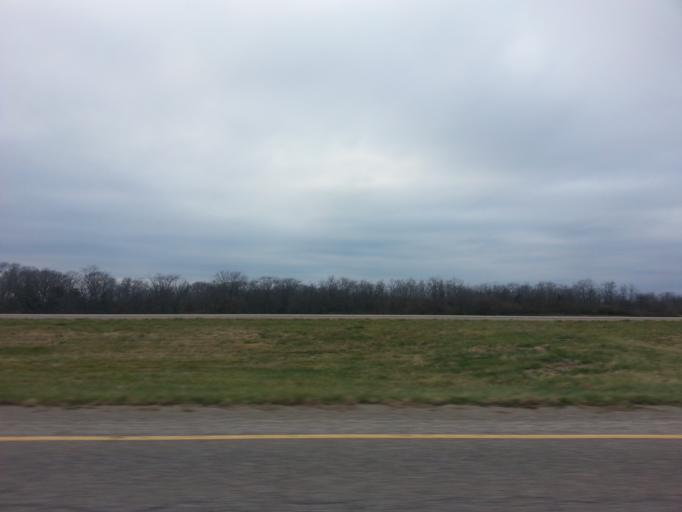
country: US
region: Iowa
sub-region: Henry County
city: Mount Pleasant
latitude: 40.9075
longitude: -91.5490
